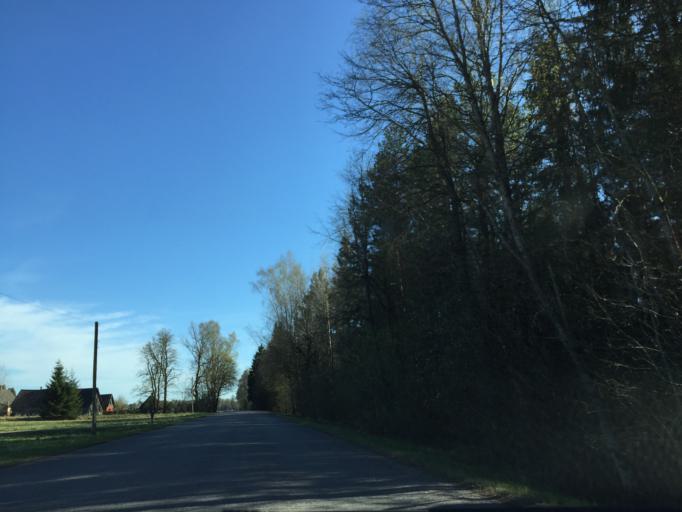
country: EE
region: Valgamaa
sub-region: Valga linn
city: Valga
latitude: 57.8610
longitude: 26.2530
